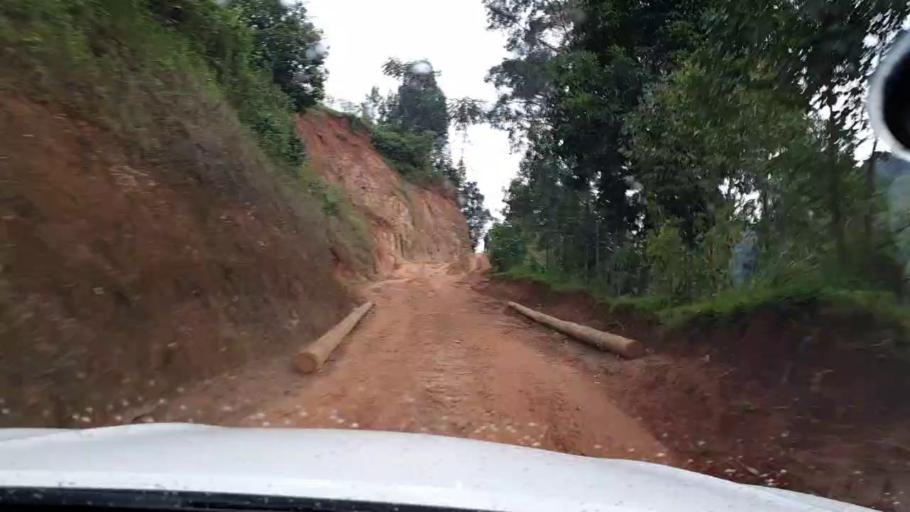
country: RW
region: Western Province
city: Cyangugu
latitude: -2.3987
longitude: 29.2306
